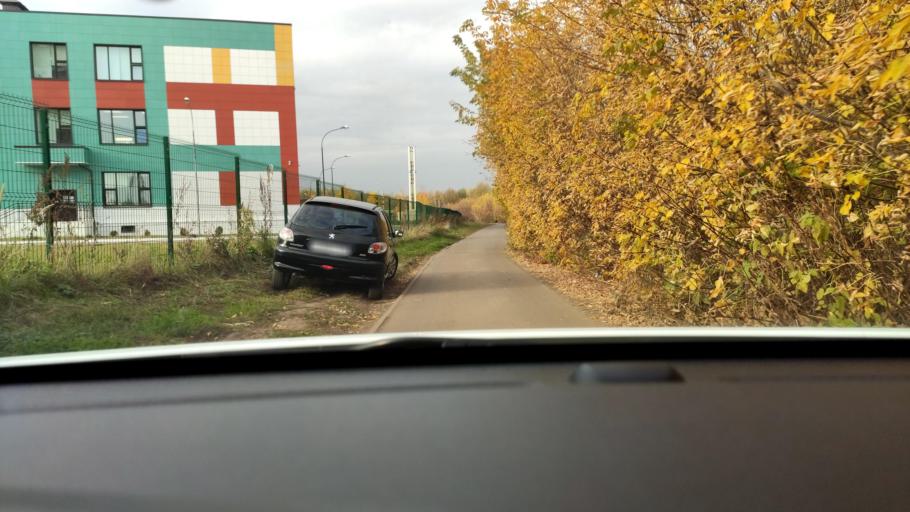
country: RU
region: Tatarstan
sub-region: Gorod Kazan'
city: Kazan
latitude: 55.8054
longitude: 49.2139
